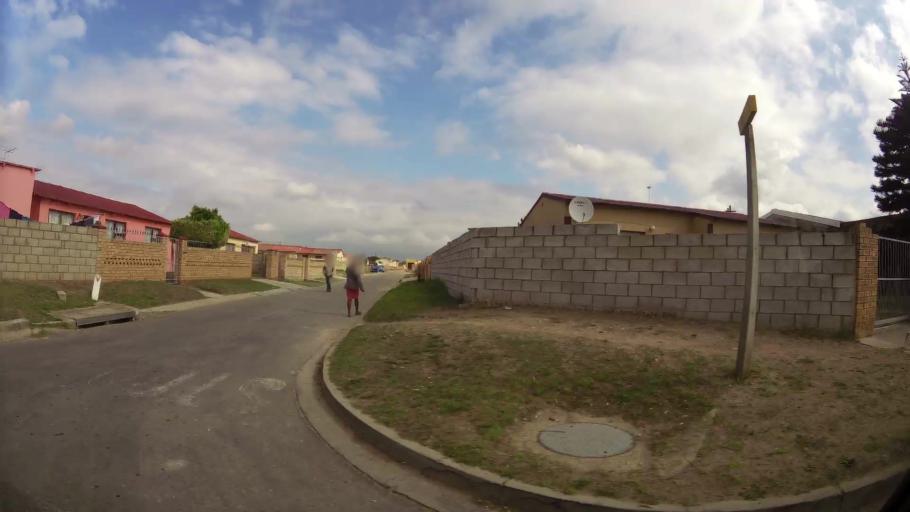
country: ZA
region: Eastern Cape
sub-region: Nelson Mandela Bay Metropolitan Municipality
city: Port Elizabeth
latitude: -33.8088
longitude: 25.5872
